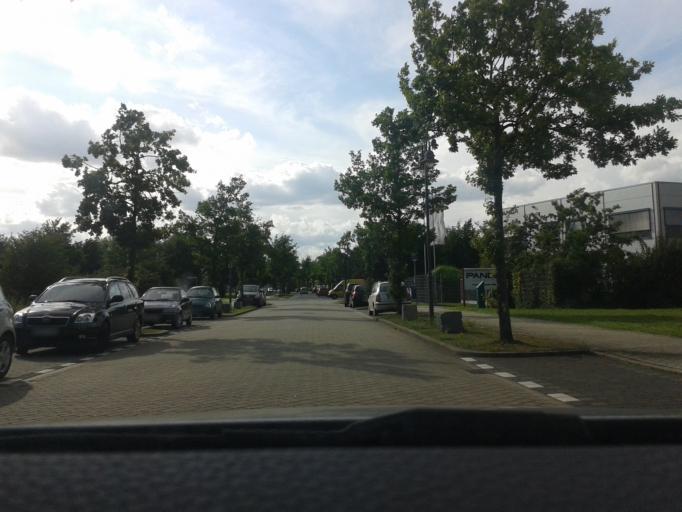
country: DE
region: North Rhine-Westphalia
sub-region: Regierungsbezirk Dusseldorf
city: Hochfeld
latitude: 51.4300
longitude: 6.6996
